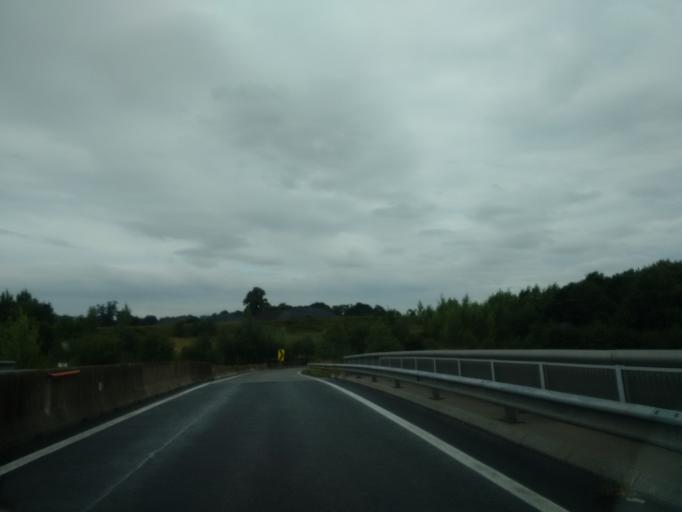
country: AT
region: Upper Austria
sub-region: Wels-Land
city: Sattledt
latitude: 48.0679
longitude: 14.0304
